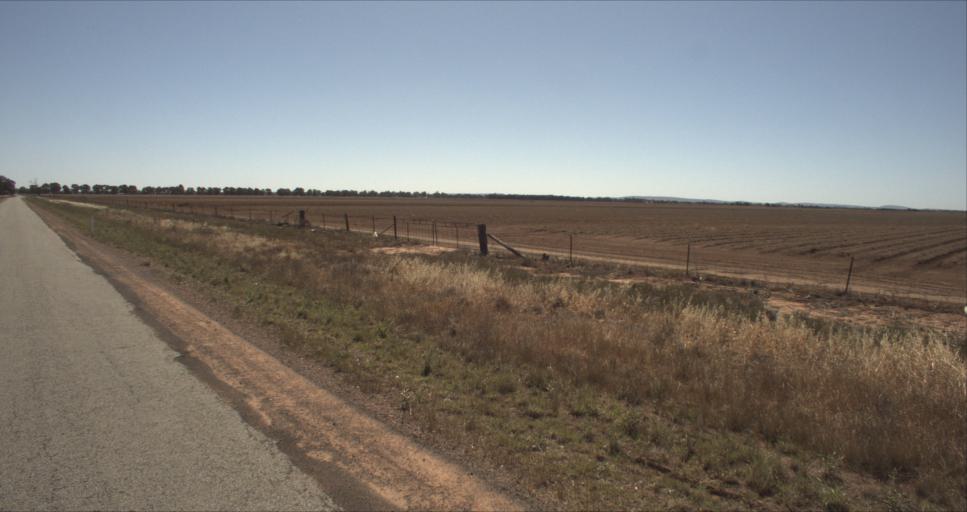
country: AU
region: New South Wales
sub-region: Leeton
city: Leeton
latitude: -34.5608
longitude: 146.3127
